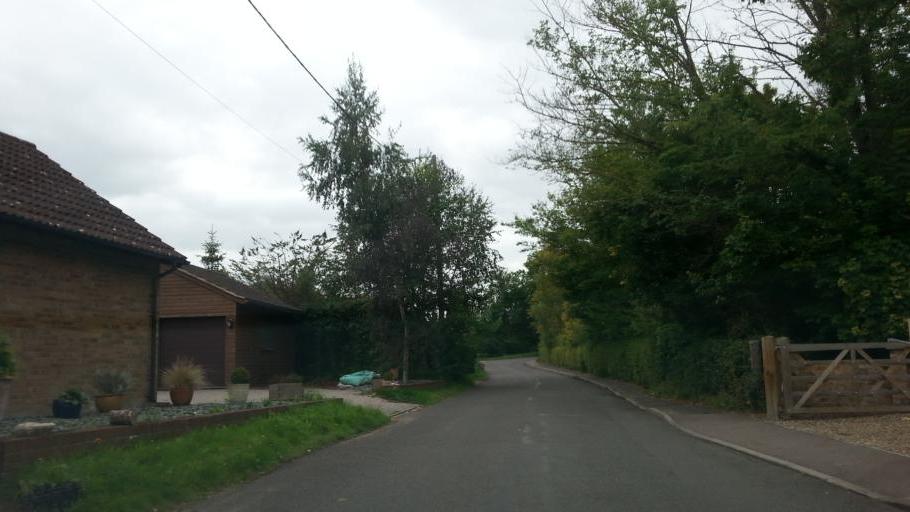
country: GB
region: England
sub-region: Cambridgeshire
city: Wimpole
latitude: 52.1346
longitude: -0.0617
